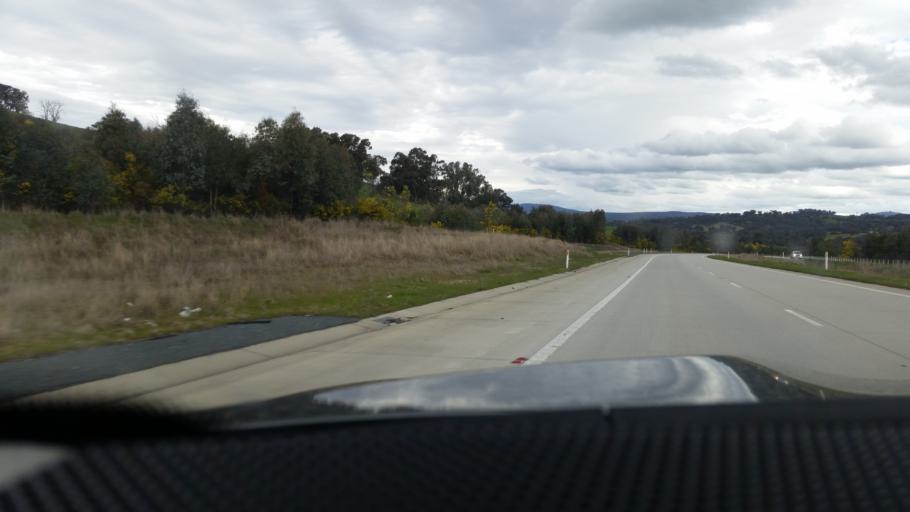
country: AU
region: New South Wales
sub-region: Greater Hume Shire
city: Holbrook
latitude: -35.8144
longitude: 147.2385
